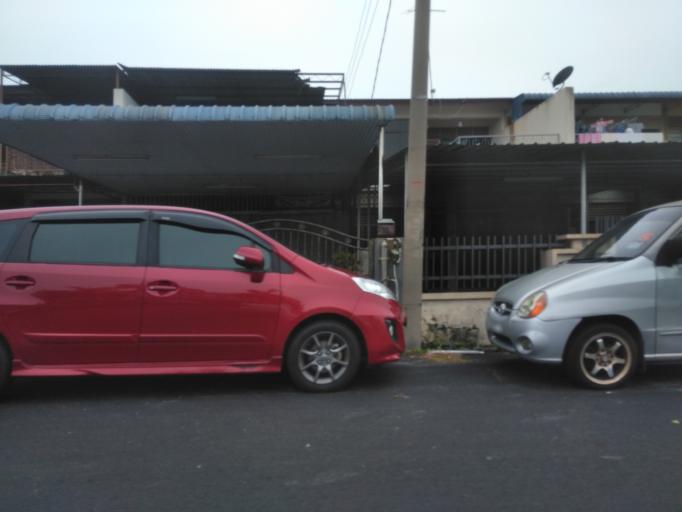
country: MY
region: Penang
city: Bukit Mertajam
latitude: 5.3619
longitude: 100.4501
